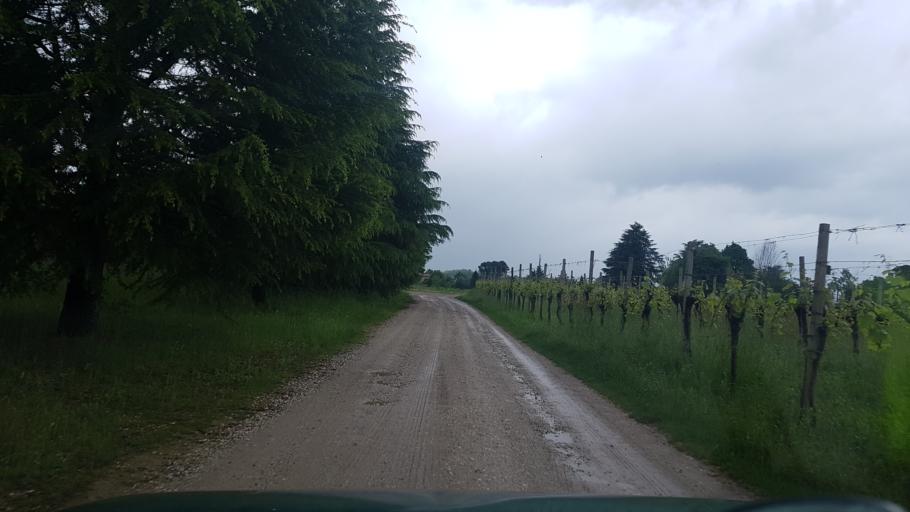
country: IT
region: Friuli Venezia Giulia
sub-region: Provincia di Gorizia
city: Mossa
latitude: 45.9318
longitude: 13.5526
